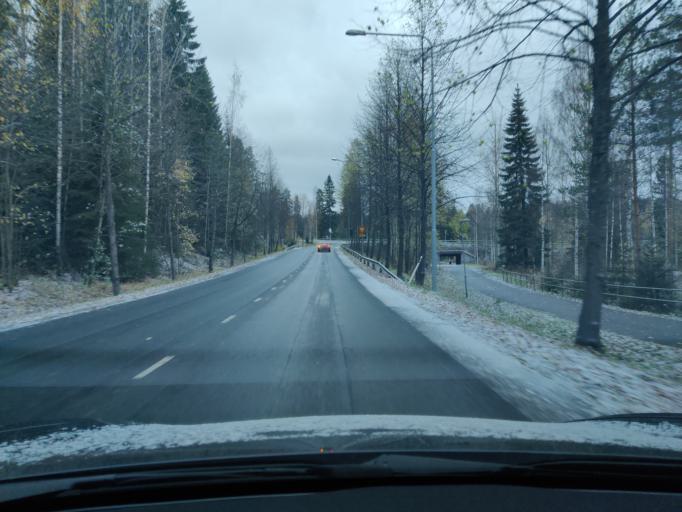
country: FI
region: Northern Savo
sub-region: Kuopio
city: Kuopio
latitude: 62.8408
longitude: 27.6346
